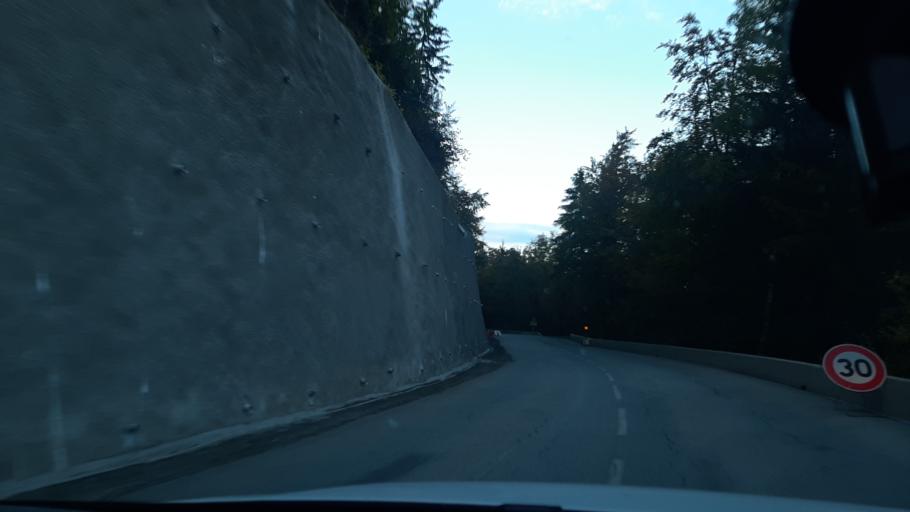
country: FR
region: Rhone-Alpes
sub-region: Departement de la Savoie
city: Saint-Jean-de-Maurienne
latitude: 45.2186
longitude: 6.3060
